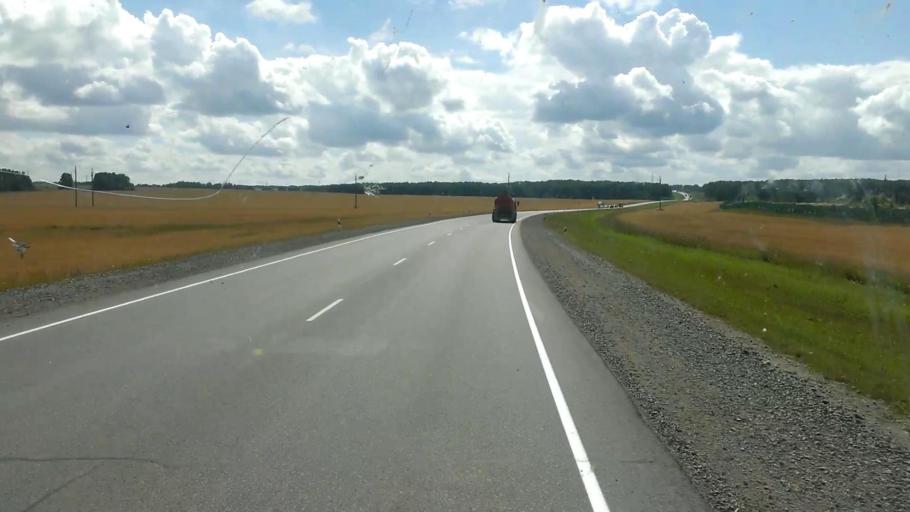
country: RU
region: Altai Krai
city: Troitskoye
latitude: 52.9933
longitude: 84.7410
